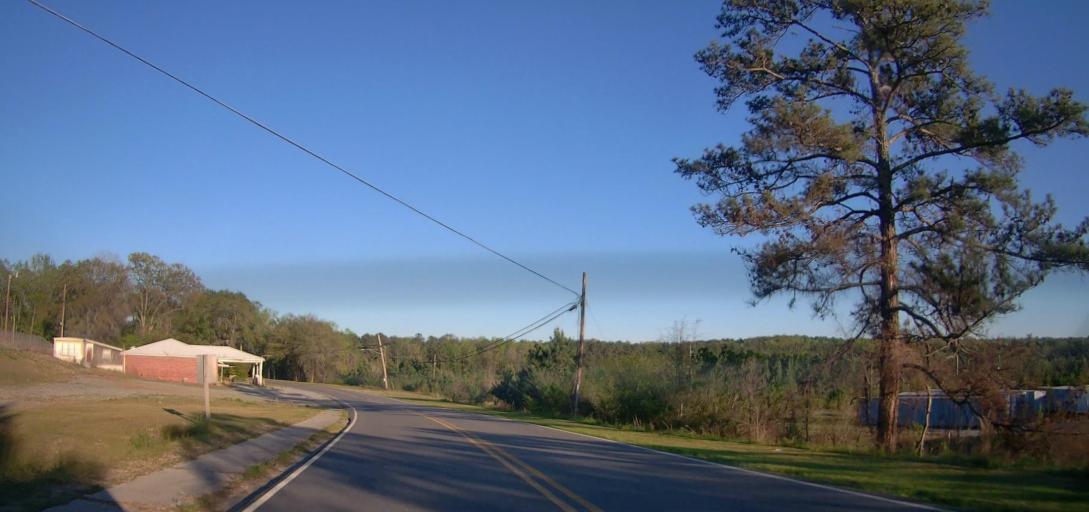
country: US
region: Georgia
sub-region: Wilkinson County
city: Irwinton
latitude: 32.8463
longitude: -83.2112
